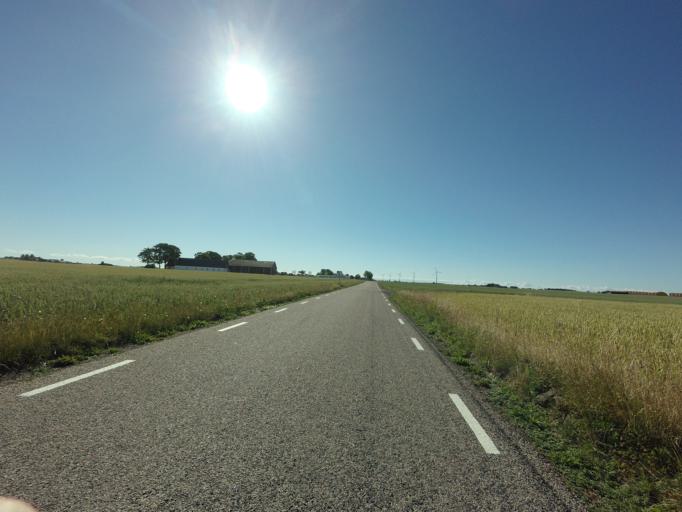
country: SE
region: Skane
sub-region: Trelleborgs Kommun
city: Skare
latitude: 55.3981
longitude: 13.0218
